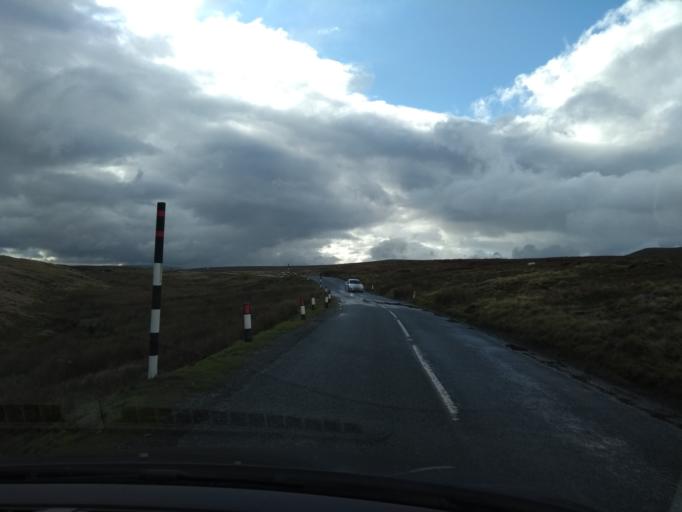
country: GB
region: England
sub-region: Cumbria
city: Kirkby Stephen
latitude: 54.3574
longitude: -2.2011
